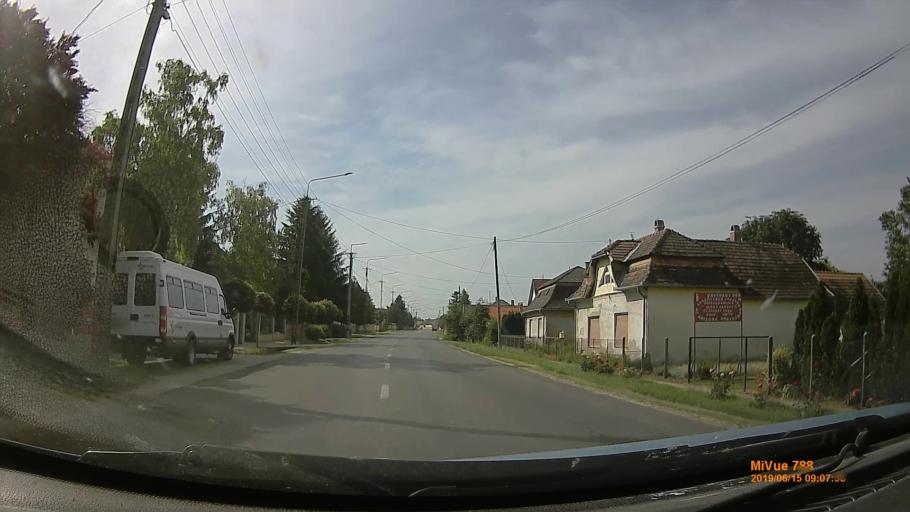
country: HU
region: Tolna
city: Iregszemcse
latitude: 46.6999
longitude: 18.1801
